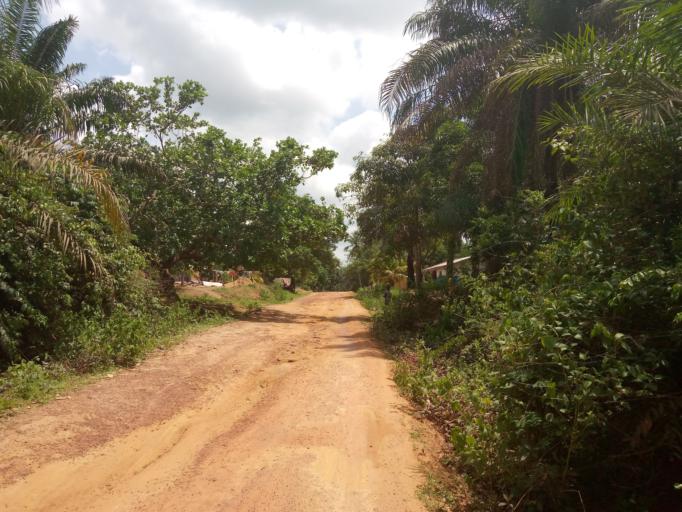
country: SL
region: Western Area
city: Waterloo
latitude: 8.3781
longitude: -12.9661
